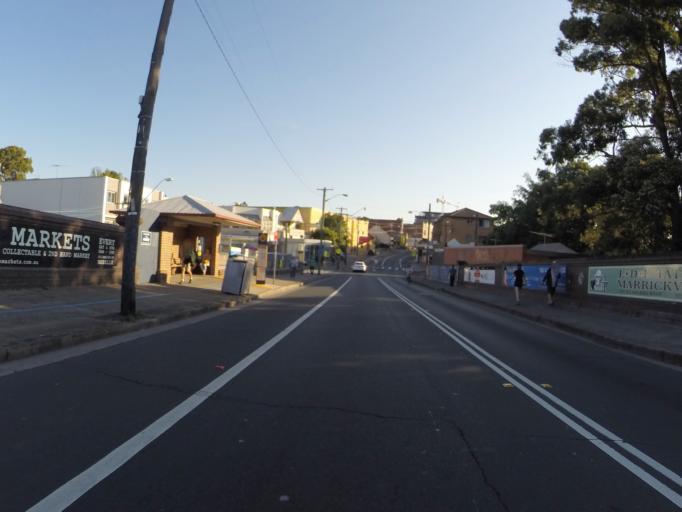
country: AU
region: New South Wales
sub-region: Marrickville
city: Marrickville
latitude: -33.9138
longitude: 151.1531
